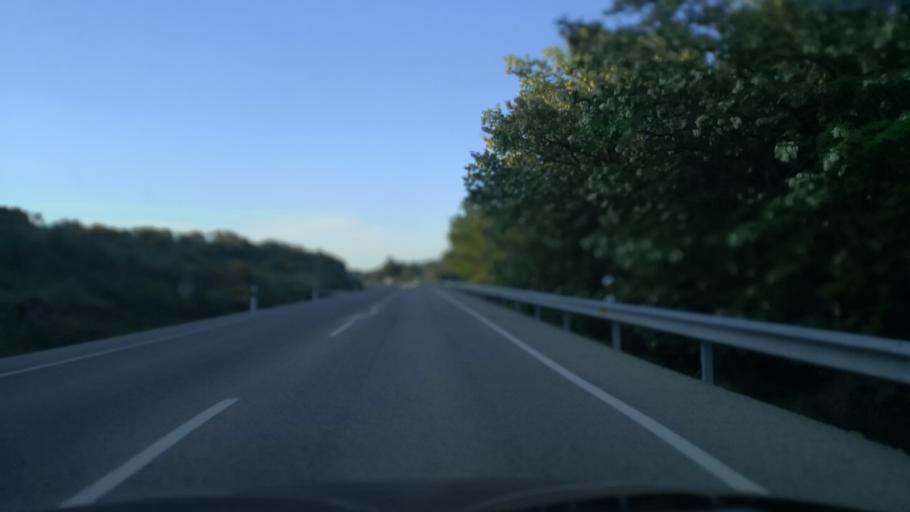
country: ES
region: Extremadura
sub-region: Provincia de Caceres
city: Valencia de Alcantara
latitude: 39.3880
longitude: -7.2471
